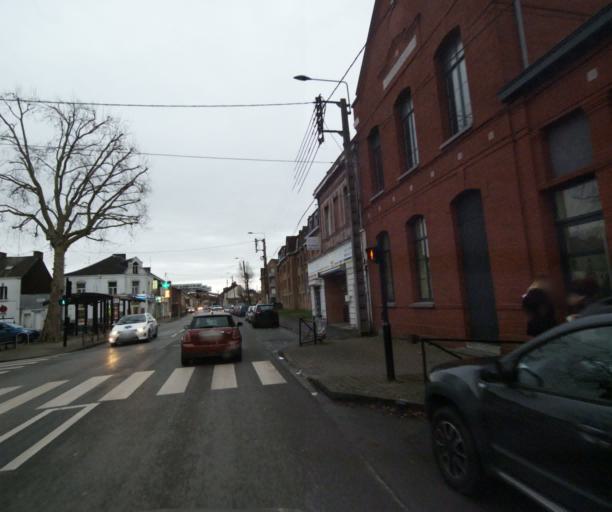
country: FR
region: Nord-Pas-de-Calais
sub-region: Departement du Nord
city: Petite-Foret
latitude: 50.3626
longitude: 3.4933
